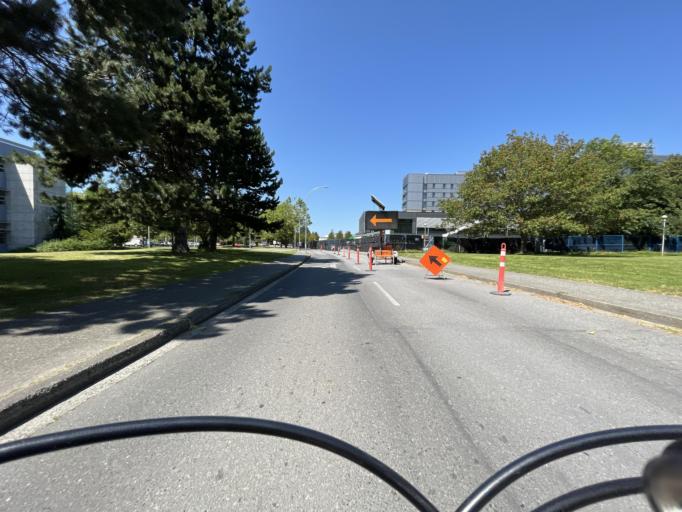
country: CA
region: British Columbia
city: Oak Bay
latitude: 48.4634
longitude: -123.3081
